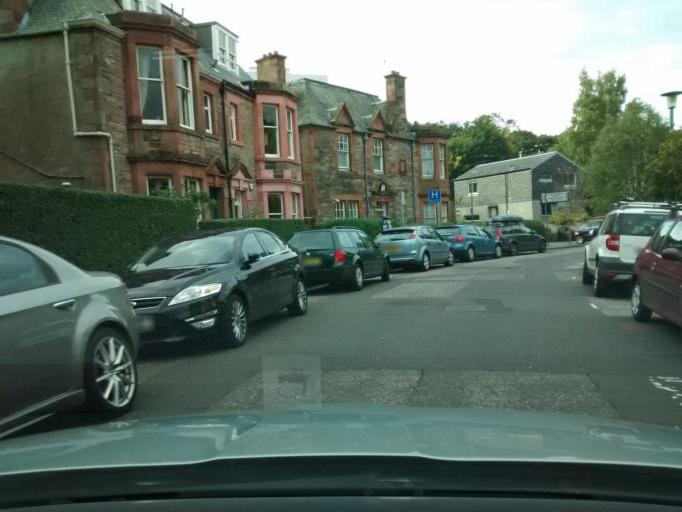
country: GB
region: Scotland
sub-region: Edinburgh
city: Edinburgh
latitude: 55.9278
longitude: -3.2115
